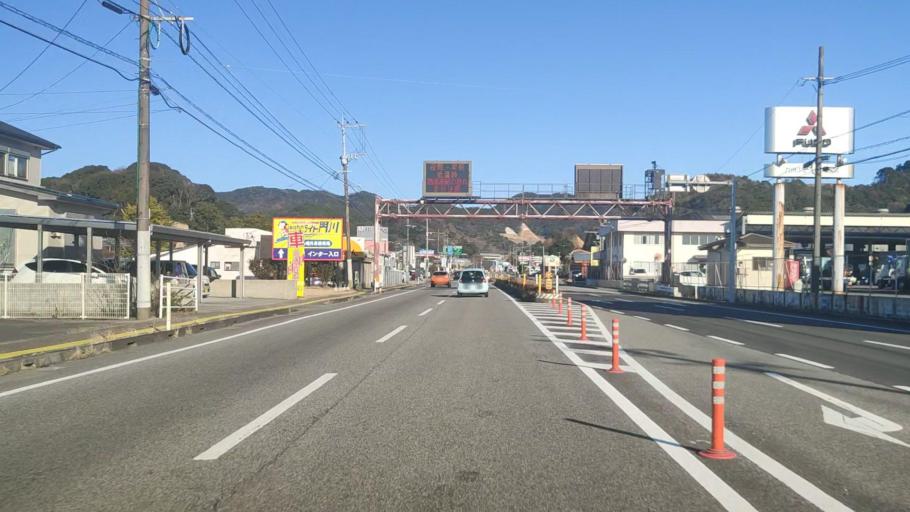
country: JP
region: Miyazaki
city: Nobeoka
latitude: 32.4918
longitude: 131.6635
